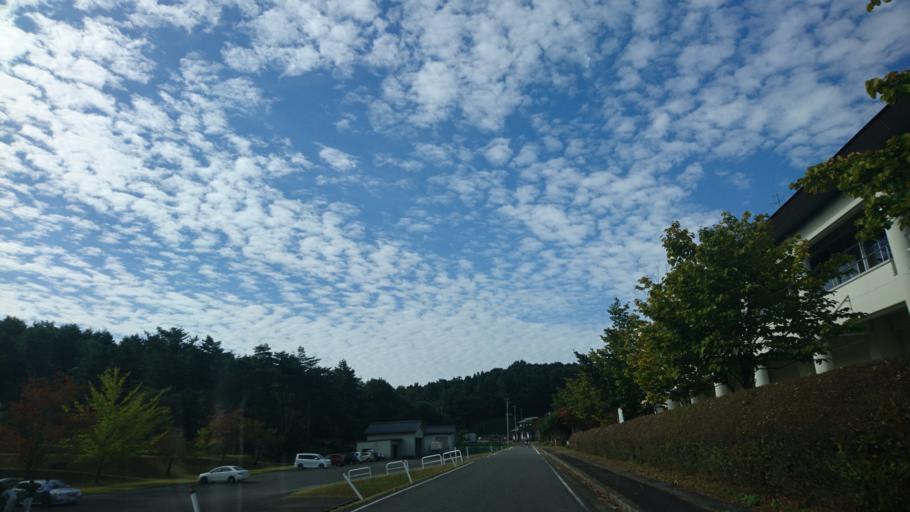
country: JP
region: Fukushima
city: Sukagawa
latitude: 37.3070
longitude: 140.2691
